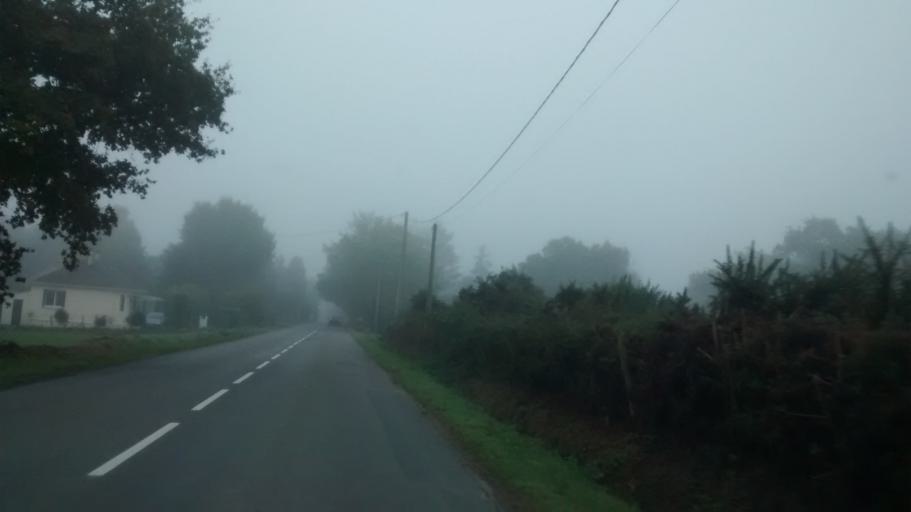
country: FR
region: Brittany
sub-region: Departement d'Ille-et-Vilaine
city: Liffre
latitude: 48.2031
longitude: -1.4950
